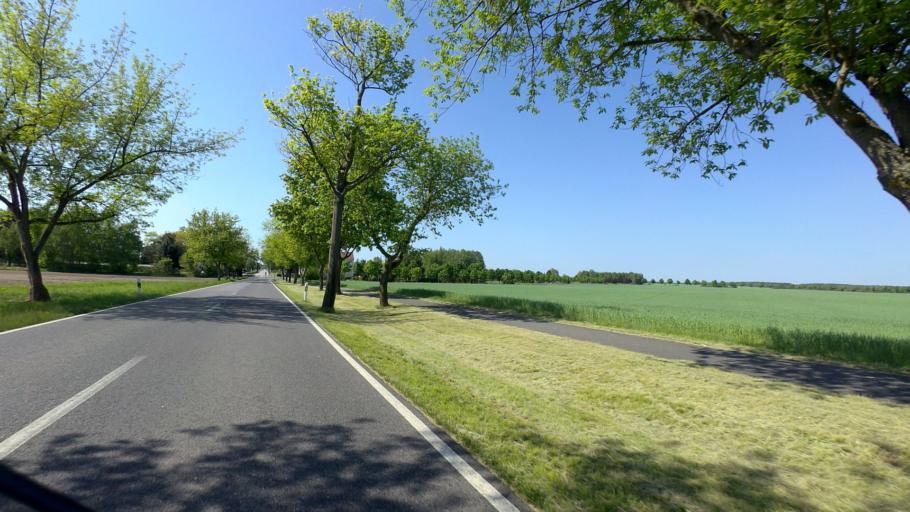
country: DE
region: Brandenburg
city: Schlepzig
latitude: 52.0425
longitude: 14.0279
